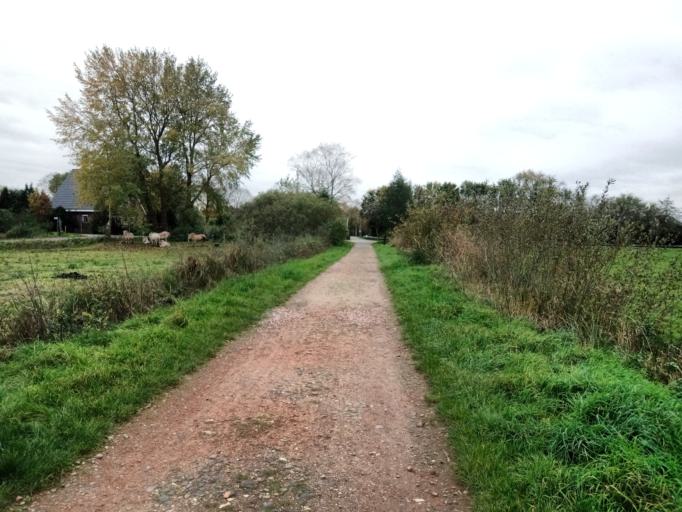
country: DE
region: Schleswig-Holstein
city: Sankt Michaelisdonn
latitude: 53.9883
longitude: 9.1214
